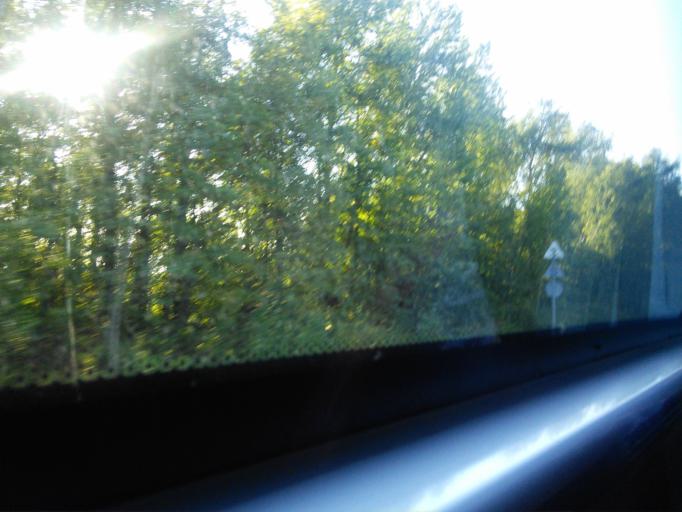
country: RU
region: Jaroslavl
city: Poshekhon'ye
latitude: 58.3661
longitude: 39.0272
